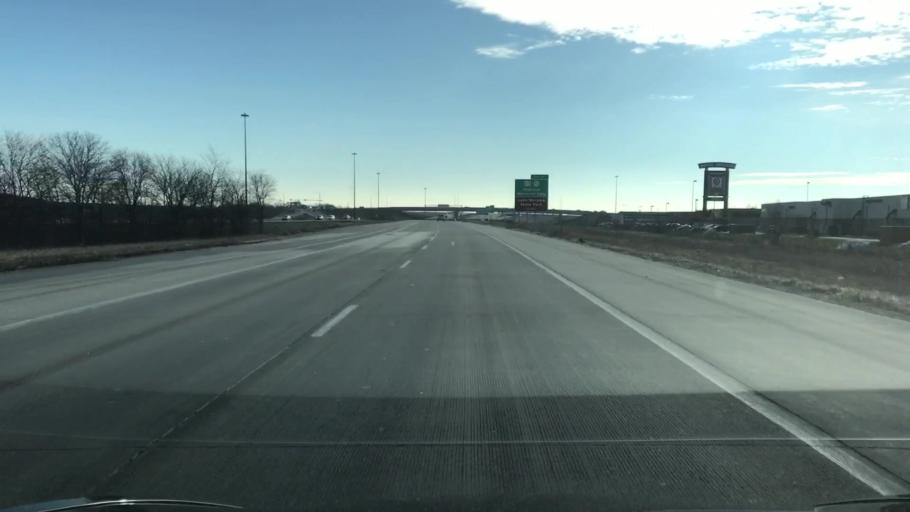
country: US
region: Iowa
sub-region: Pottawattamie County
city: Council Bluffs
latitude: 41.2252
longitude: -95.8375
